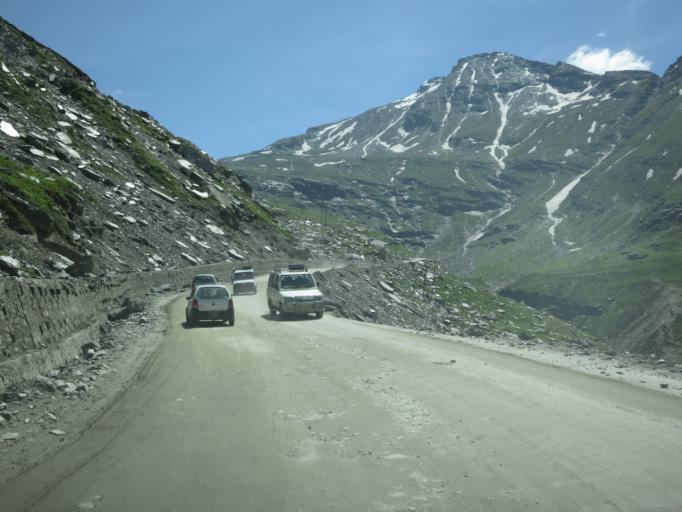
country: IN
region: Himachal Pradesh
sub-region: Kulu
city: Manali
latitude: 32.3558
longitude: 77.2265
